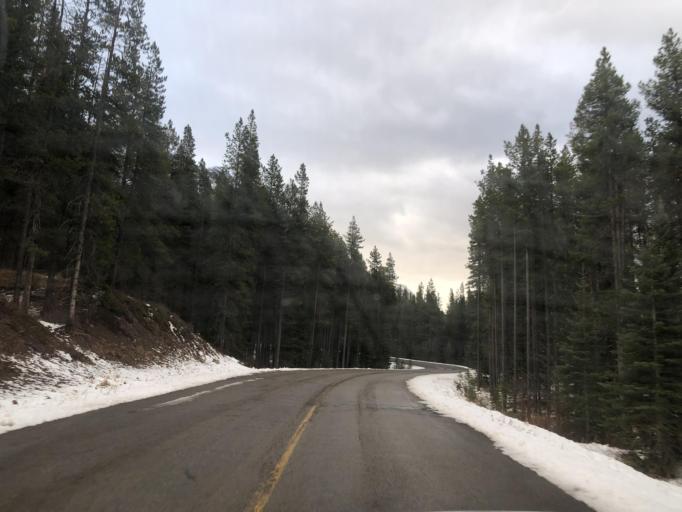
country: CA
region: Alberta
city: Canmore
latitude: 50.7118
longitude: -115.1169
